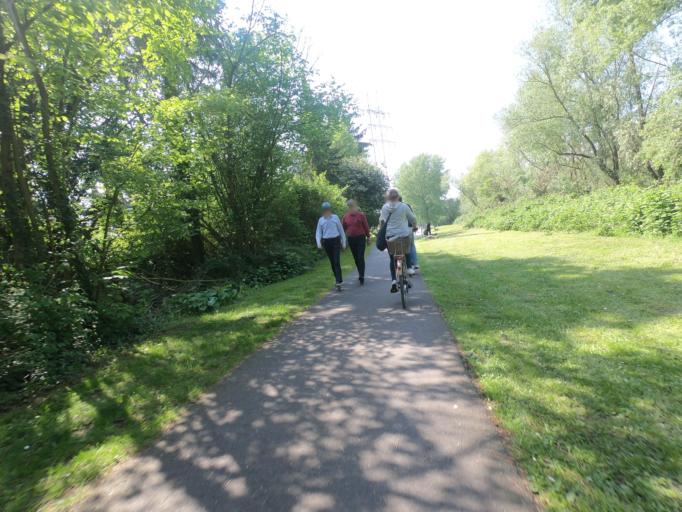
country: DE
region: Hesse
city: Kelsterbach
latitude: 50.0976
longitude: 8.5583
